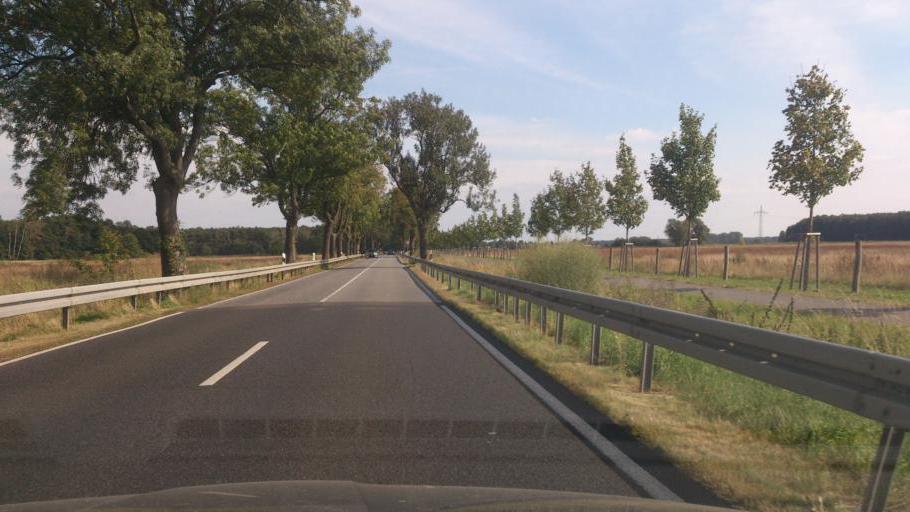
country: DE
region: Brandenburg
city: Stahnsdorf
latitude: 52.3269
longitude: 13.1774
